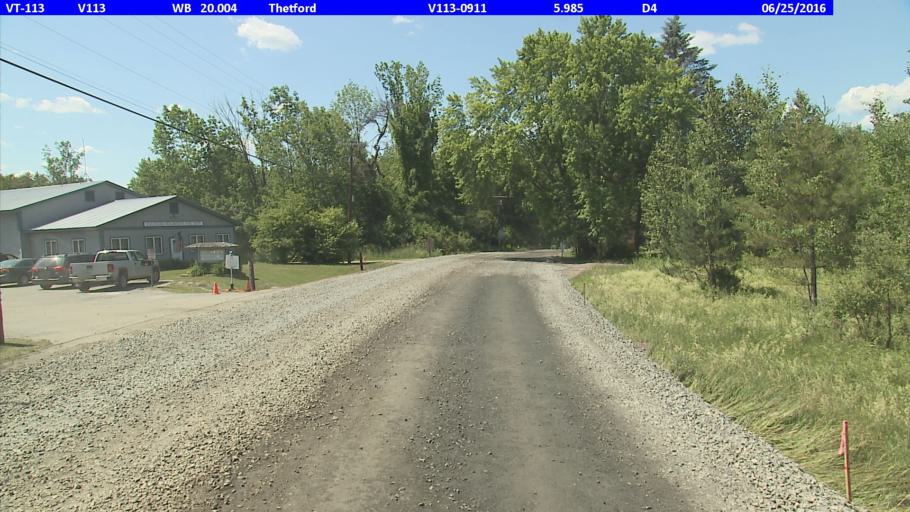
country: US
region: New Hampshire
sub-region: Grafton County
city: Lyme
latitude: 43.8209
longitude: -72.2332
